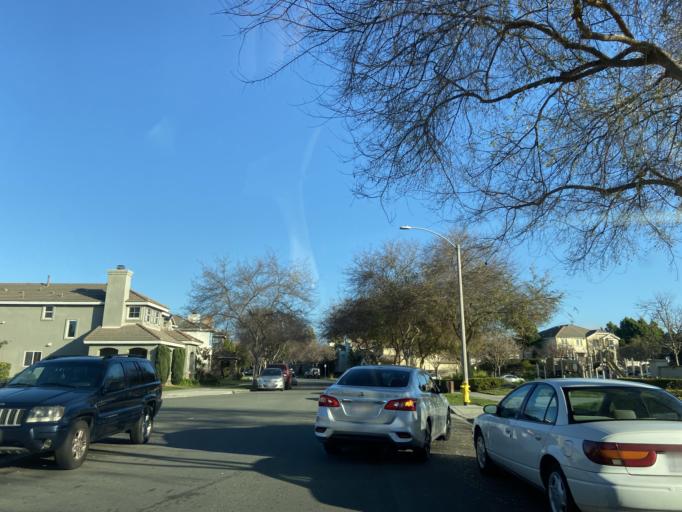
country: US
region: California
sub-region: San Diego County
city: Bonita
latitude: 32.6287
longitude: -116.9750
